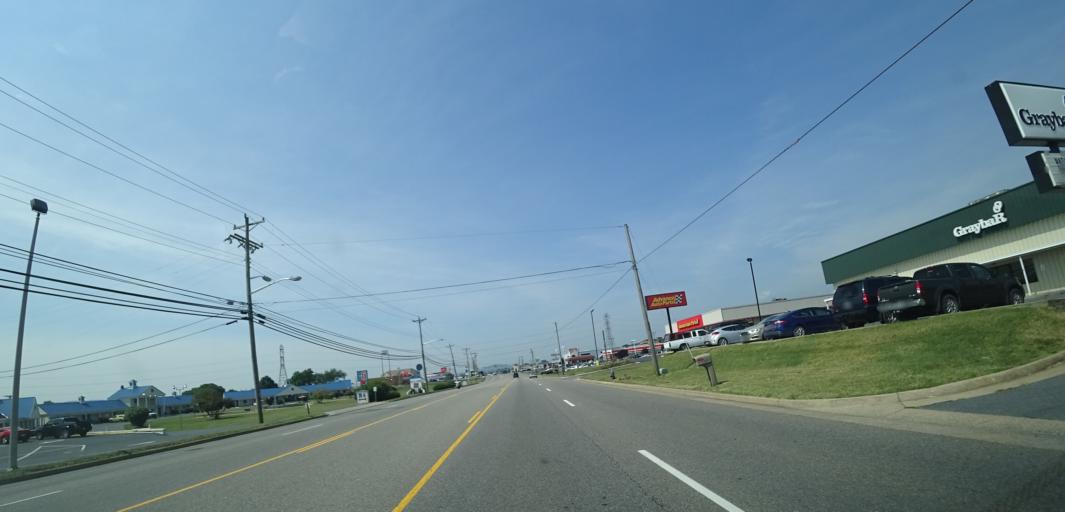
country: US
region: Virginia
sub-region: Rockingham County
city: Dayton
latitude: 38.4094
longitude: -78.9050
